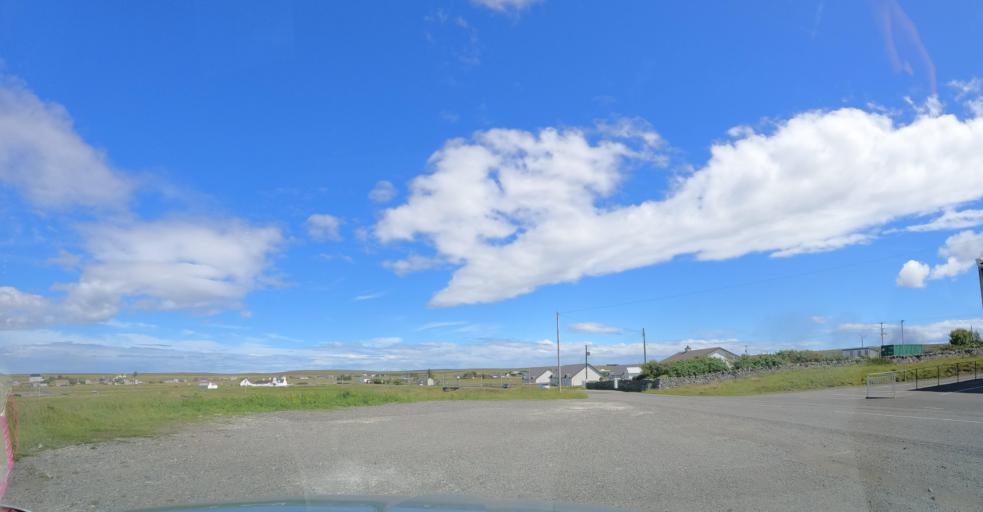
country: GB
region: Scotland
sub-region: Eilean Siar
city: Isle of Lewis
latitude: 58.3489
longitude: -6.5256
